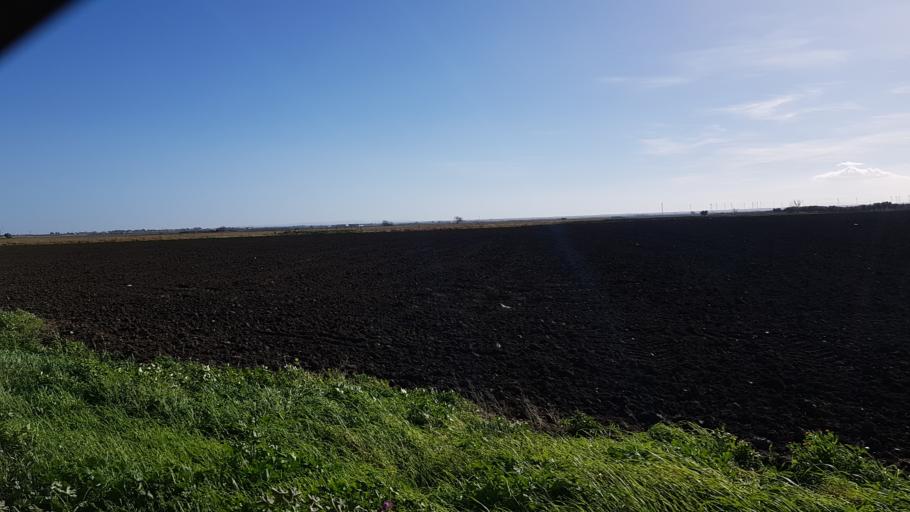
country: IT
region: Apulia
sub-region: Provincia di Foggia
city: Carapelle
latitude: 41.3821
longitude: 15.6453
